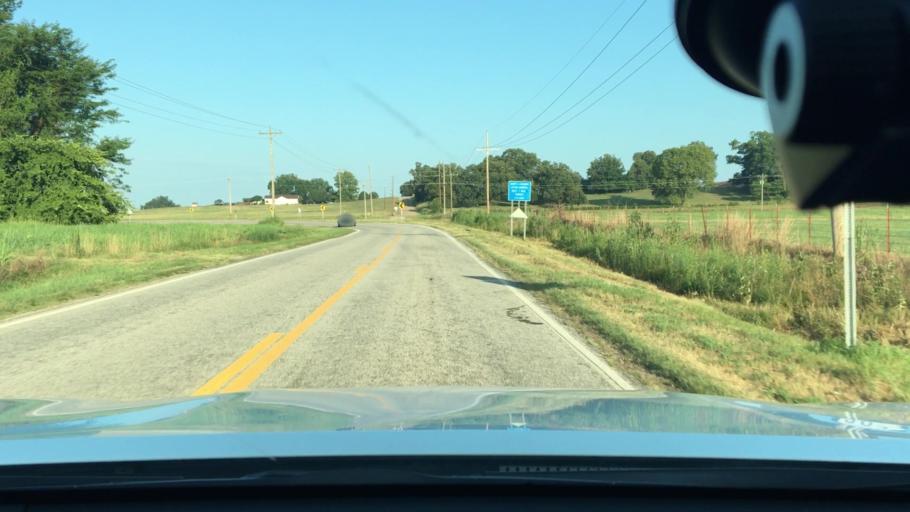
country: US
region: Arkansas
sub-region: Johnson County
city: Coal Hill
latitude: 35.3377
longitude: -93.6292
